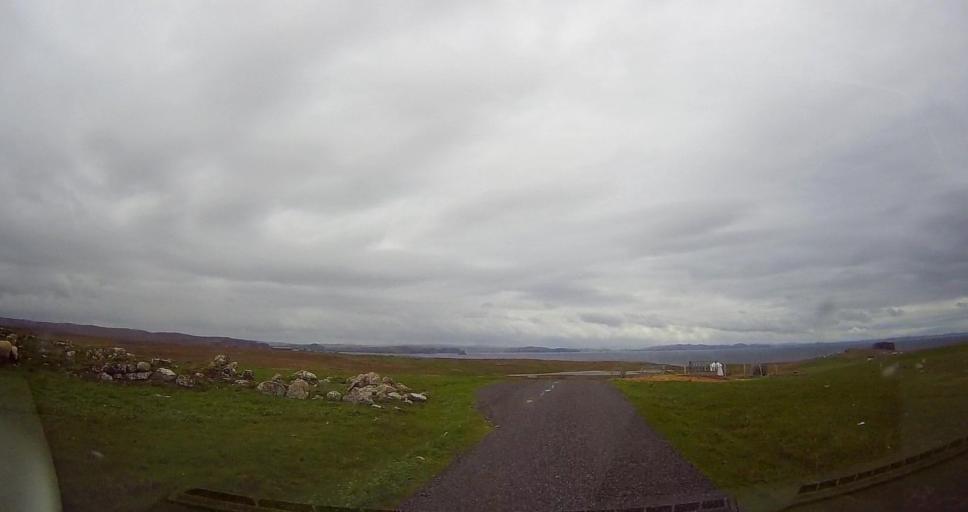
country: GB
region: Scotland
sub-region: Shetland Islands
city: Lerwick
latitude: 60.4883
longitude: -1.6167
